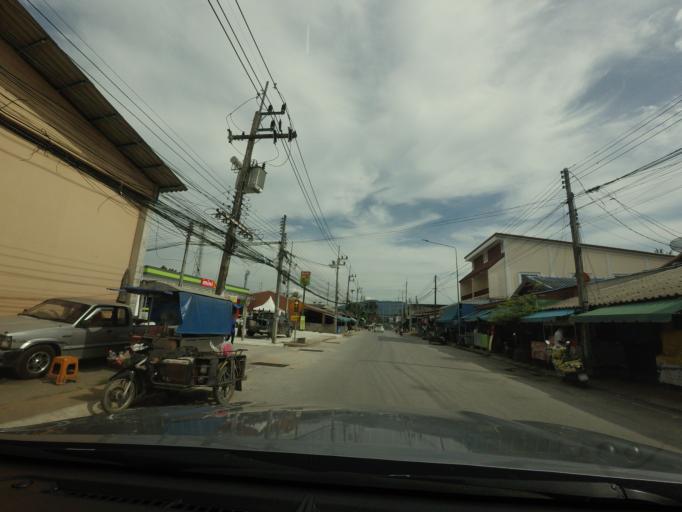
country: TH
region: Yala
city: Yala
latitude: 6.5376
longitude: 101.2930
